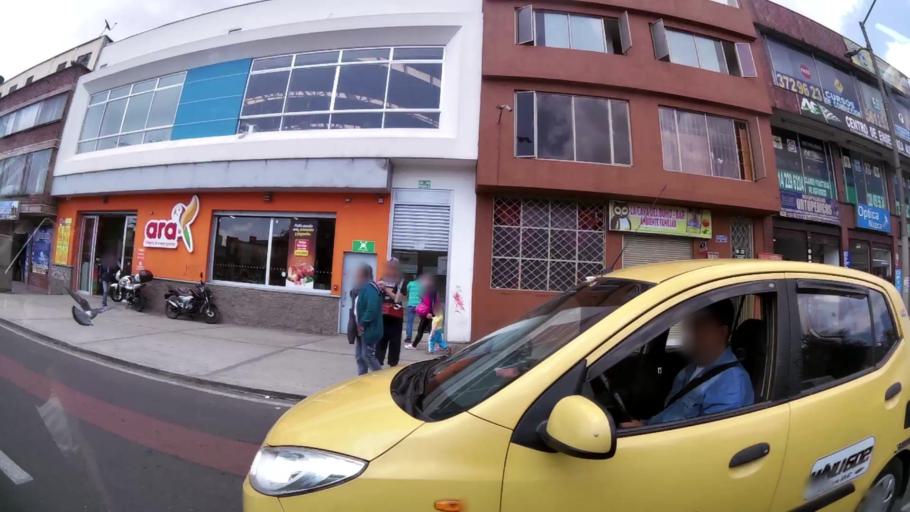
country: CO
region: Bogota D.C.
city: Bogota
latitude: 4.5829
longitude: -74.1039
